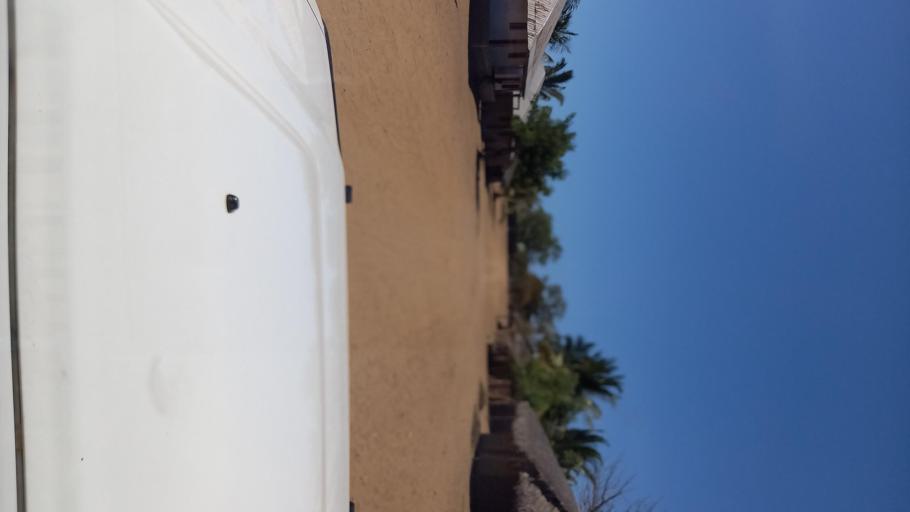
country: MZ
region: Cabo Delgado
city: Pemba
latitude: -13.4154
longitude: 40.5247
